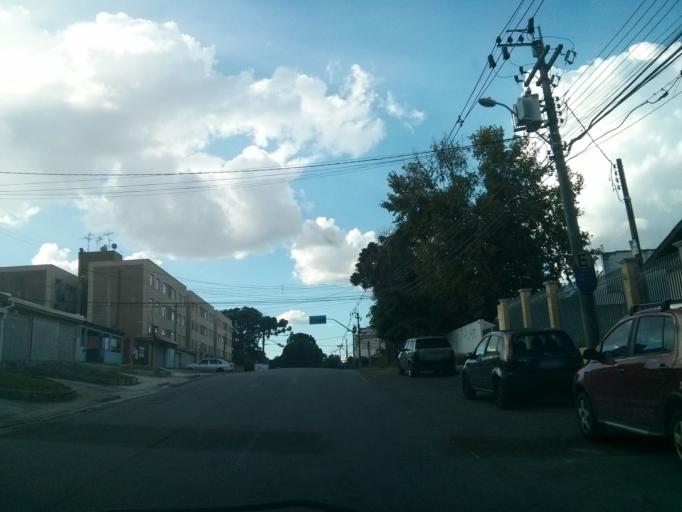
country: BR
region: Parana
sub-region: Sao Jose Dos Pinhais
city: Sao Jose dos Pinhais
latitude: -25.5232
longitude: -49.2394
